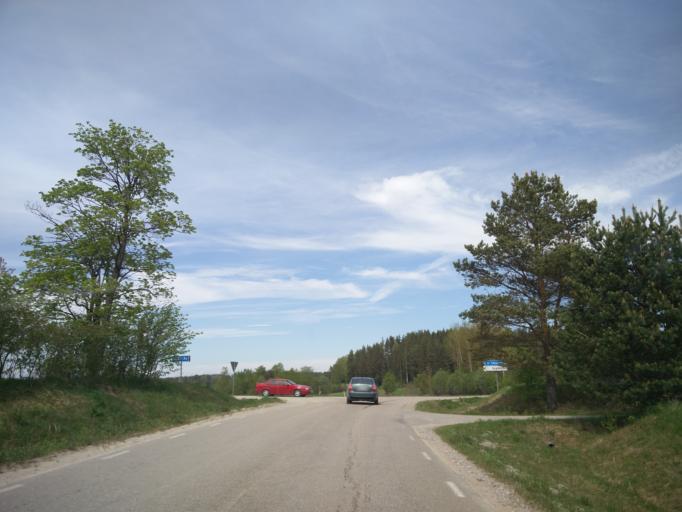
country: SE
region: Gaevleborg
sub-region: Hudiksvalls Kommun
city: Sorforsa
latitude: 61.6985
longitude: 16.9315
